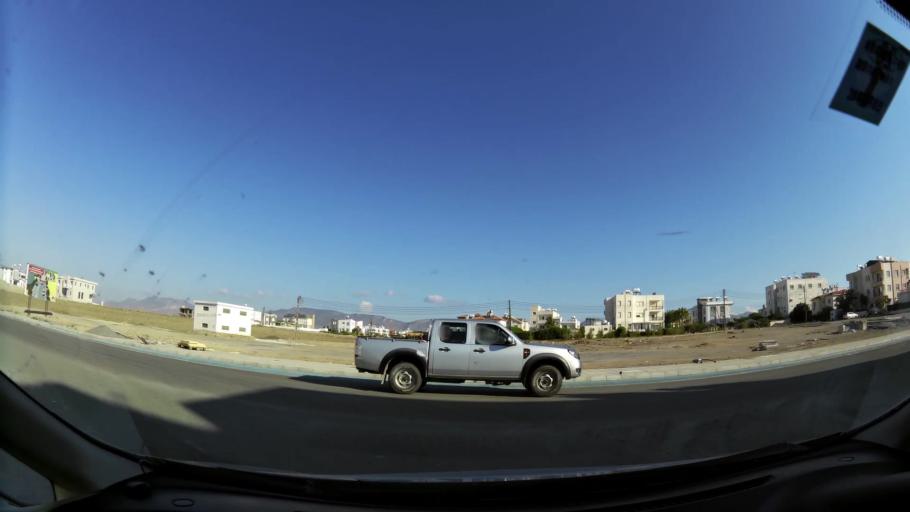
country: CY
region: Lefkosia
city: Nicosia
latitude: 35.2144
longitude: 33.2935
